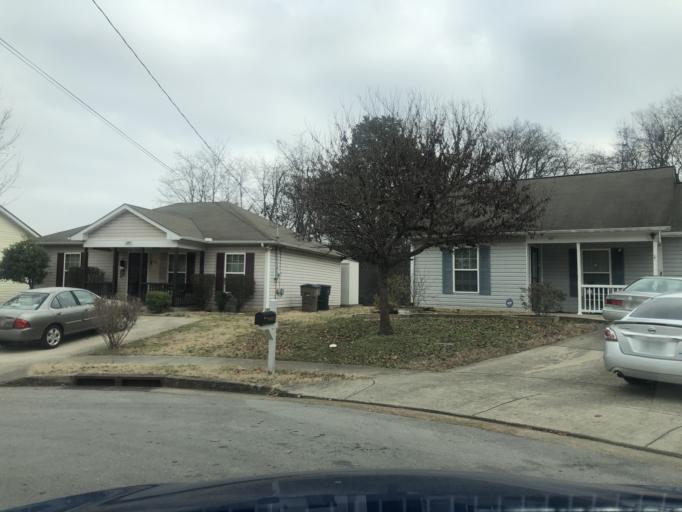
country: US
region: Tennessee
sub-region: Davidson County
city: Oak Hill
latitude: 36.0890
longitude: -86.7061
